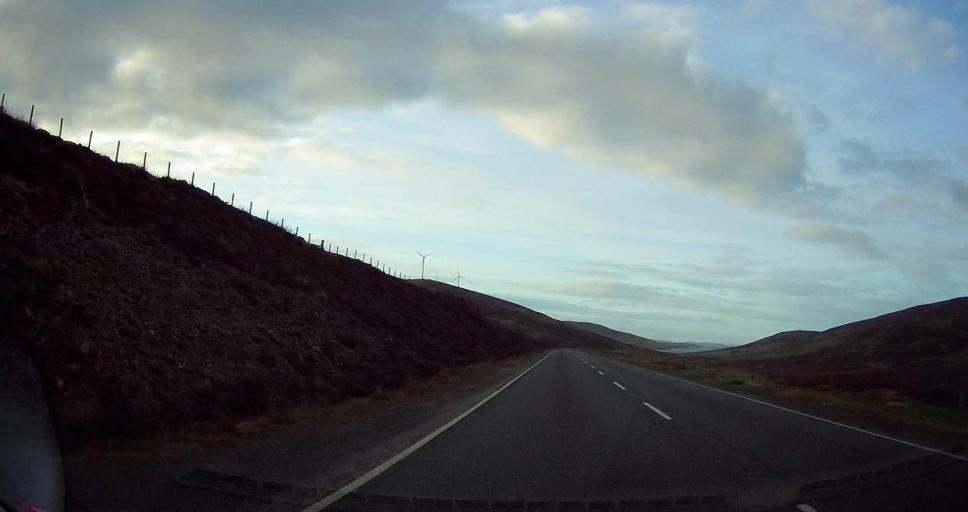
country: GB
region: Scotland
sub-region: Shetland Islands
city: Lerwick
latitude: 60.1502
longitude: -1.2381
